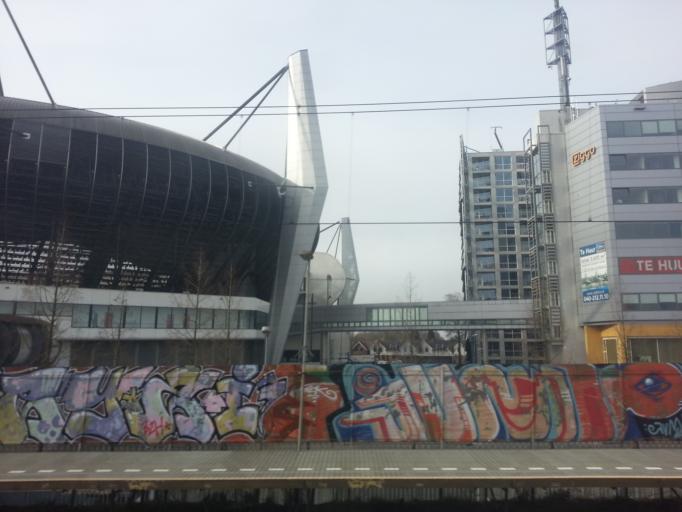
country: NL
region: North Brabant
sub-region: Gemeente Eindhoven
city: Eindhoven
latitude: 51.4431
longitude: 5.4671
